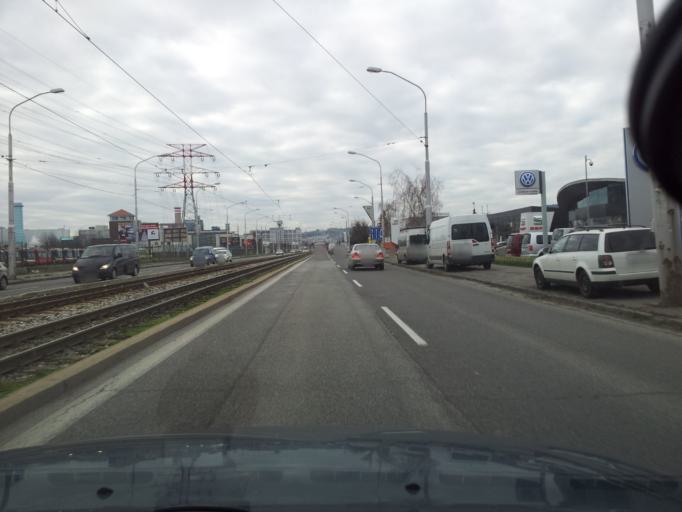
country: SK
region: Bratislavsky
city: Bratislava
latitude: 48.1818
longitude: 17.1600
